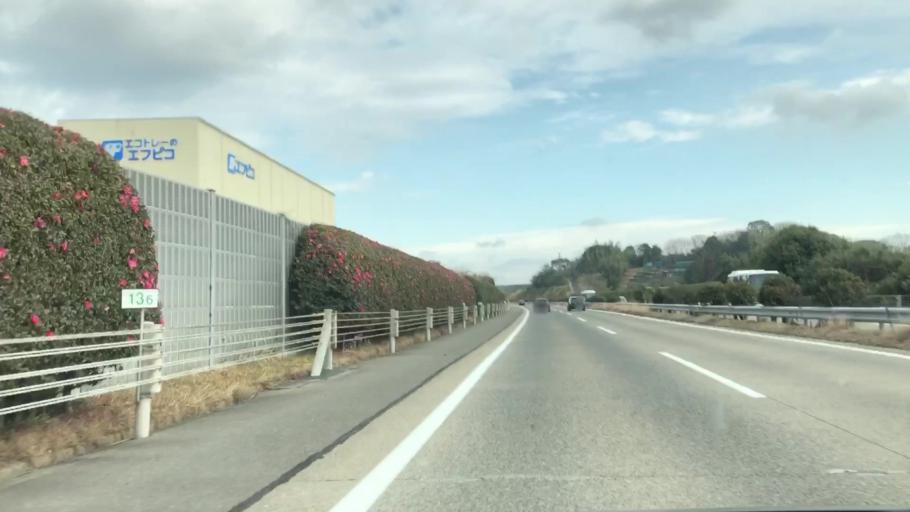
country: JP
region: Saga Prefecture
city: Kanzakimachi-kanzaki
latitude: 33.3542
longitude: 130.4086
